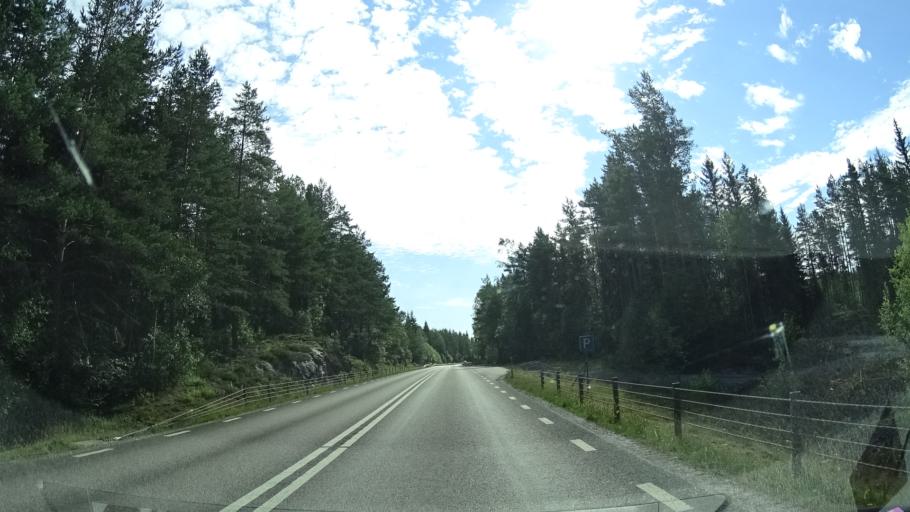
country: SE
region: Vaermland
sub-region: Arjangs Kommun
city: Toecksfors
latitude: 59.4980
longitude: 11.9056
